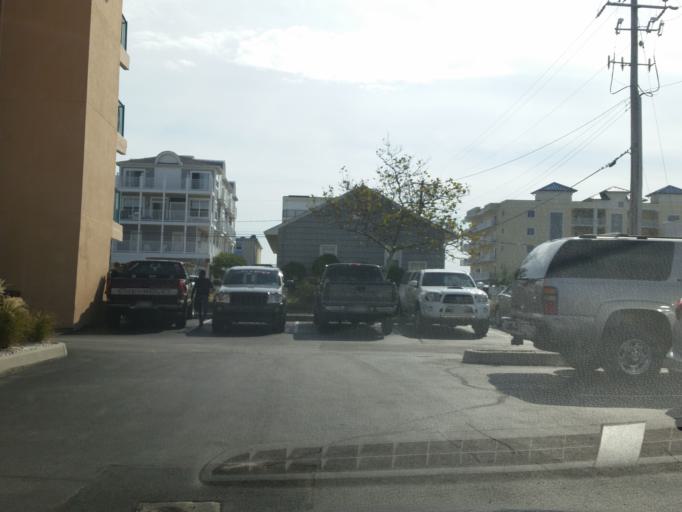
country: US
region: Maryland
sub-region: Worcester County
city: Ocean City
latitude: 38.4306
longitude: -75.0548
